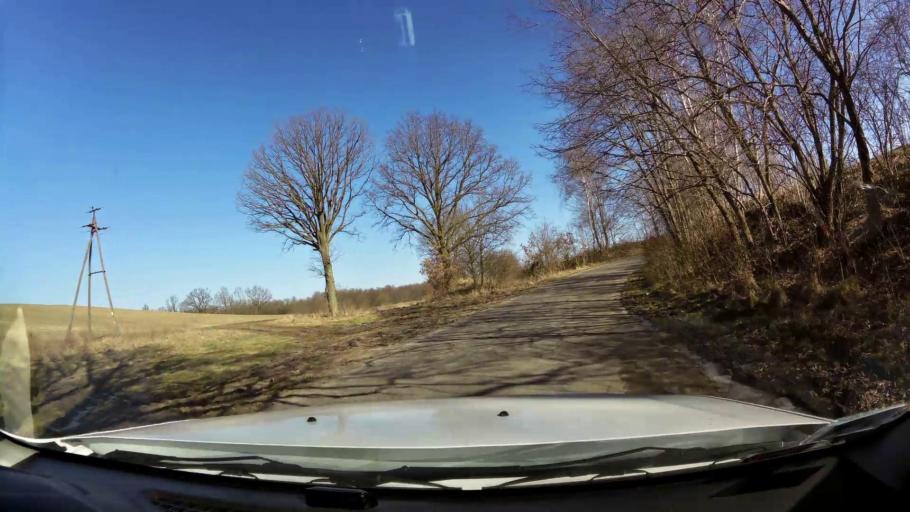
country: PL
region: West Pomeranian Voivodeship
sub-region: Powiat gryfinski
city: Banie
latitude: 53.1386
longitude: 14.6170
